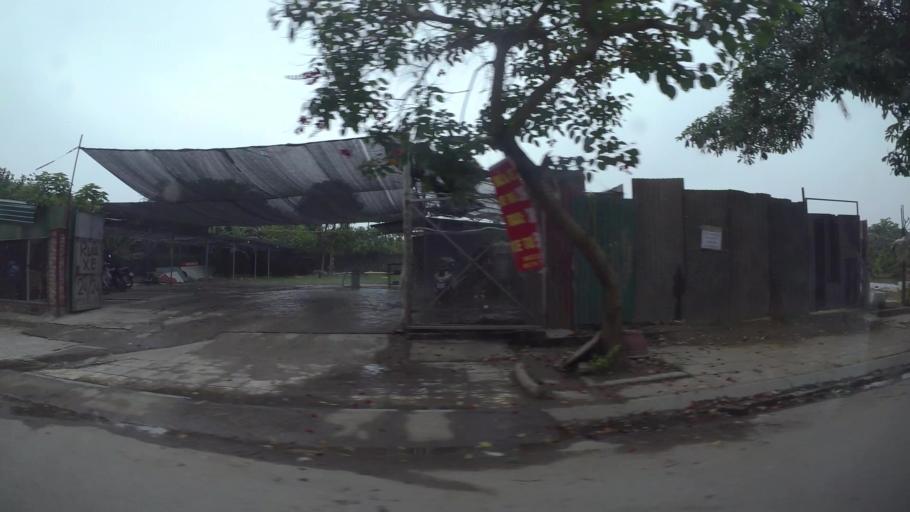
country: VN
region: Ha Noi
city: Tay Ho
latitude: 21.0575
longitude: 105.8227
